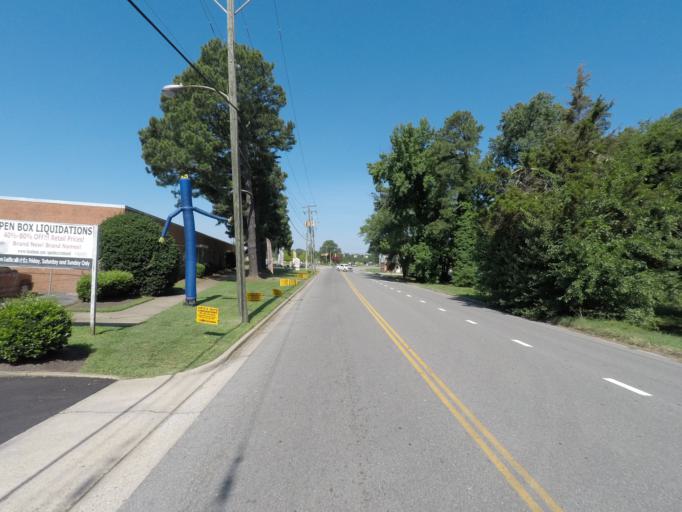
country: US
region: Virginia
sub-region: Henrico County
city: Dumbarton
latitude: 37.5923
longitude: -77.4913
